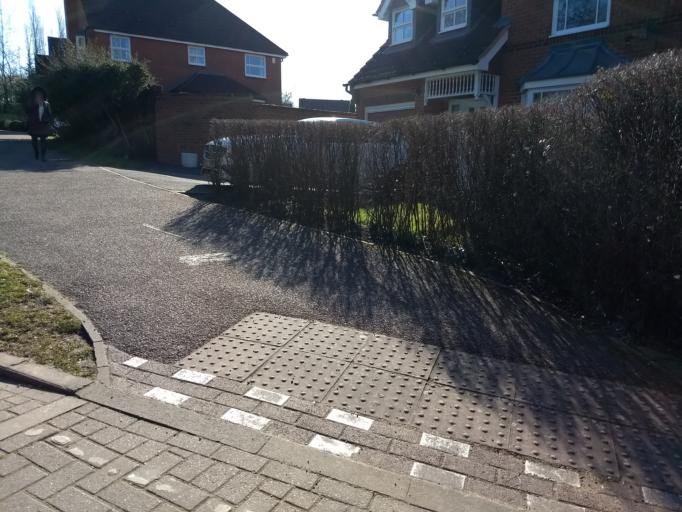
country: GB
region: England
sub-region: Milton Keynes
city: Shenley Church End
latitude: 52.0001
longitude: -0.7933
